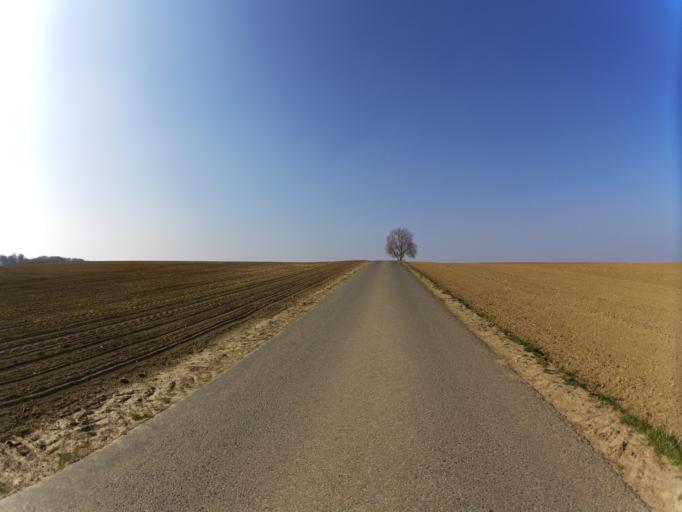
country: DE
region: Bavaria
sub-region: Regierungsbezirk Unterfranken
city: Gaukonigshofen
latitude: 49.6585
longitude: 9.9949
